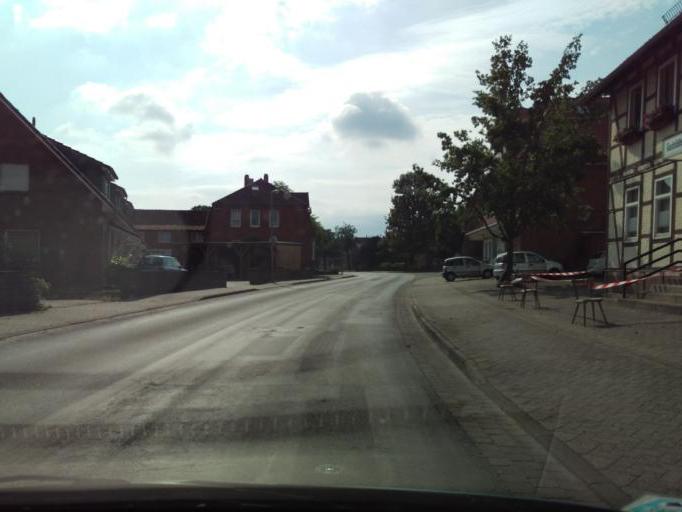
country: DE
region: Lower Saxony
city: Arpke
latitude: 52.3735
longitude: 10.1302
